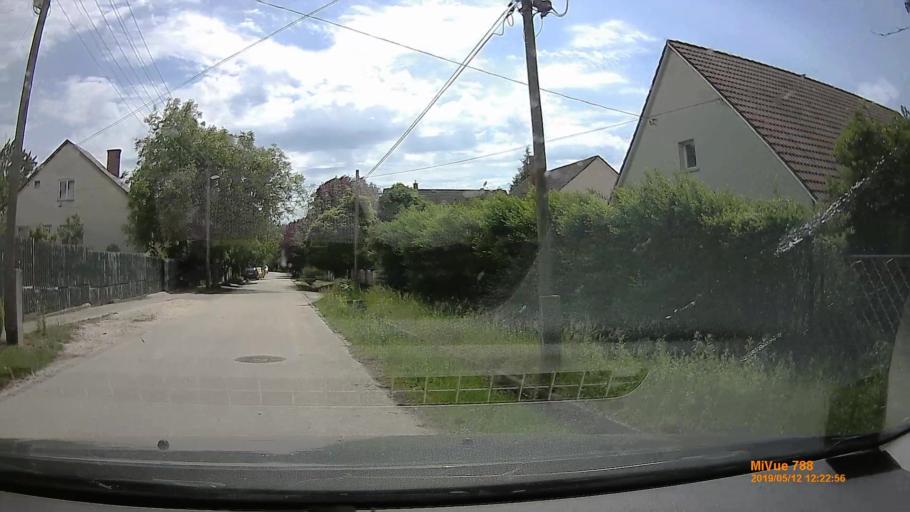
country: HU
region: Pest
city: Ecser
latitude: 47.4595
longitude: 19.2940
